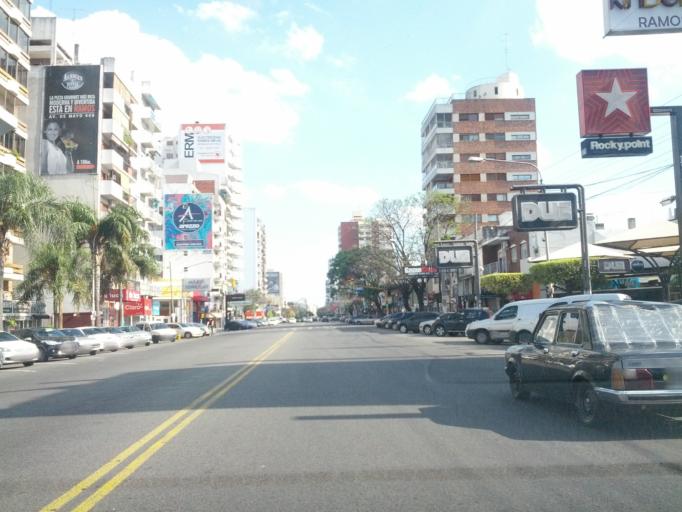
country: AR
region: Buenos Aires
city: San Justo
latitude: -34.6438
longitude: -58.5651
